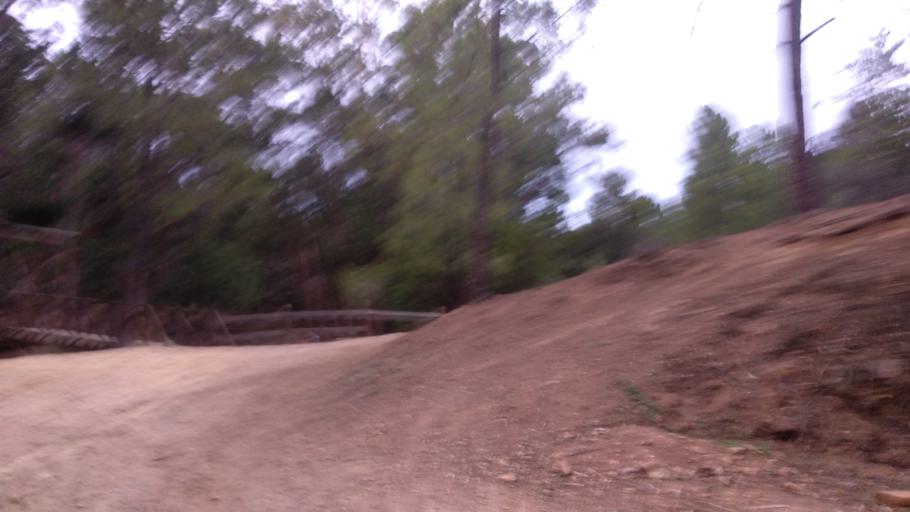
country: PT
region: Faro
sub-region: Sao Bras de Alportel
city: Sao Bras de Alportel
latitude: 37.1854
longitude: -7.9142
